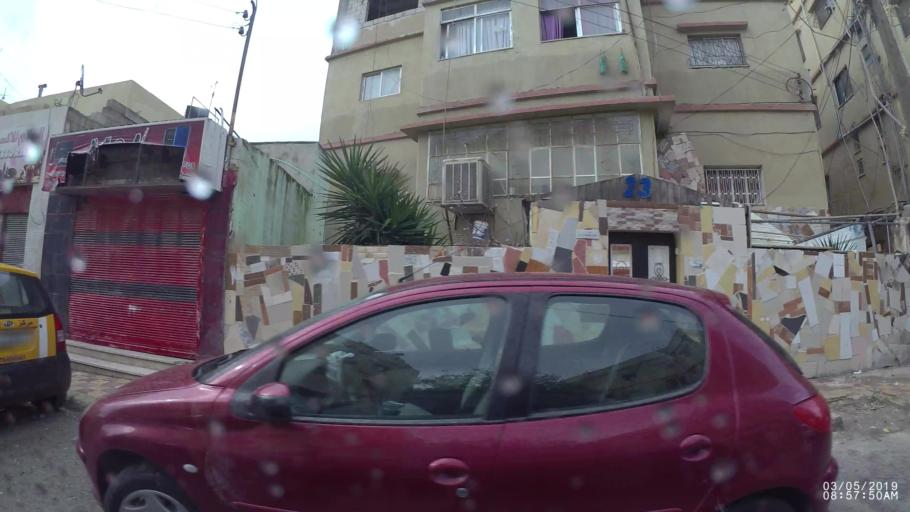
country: JO
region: Amman
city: Amman
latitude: 31.9581
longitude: 35.9388
